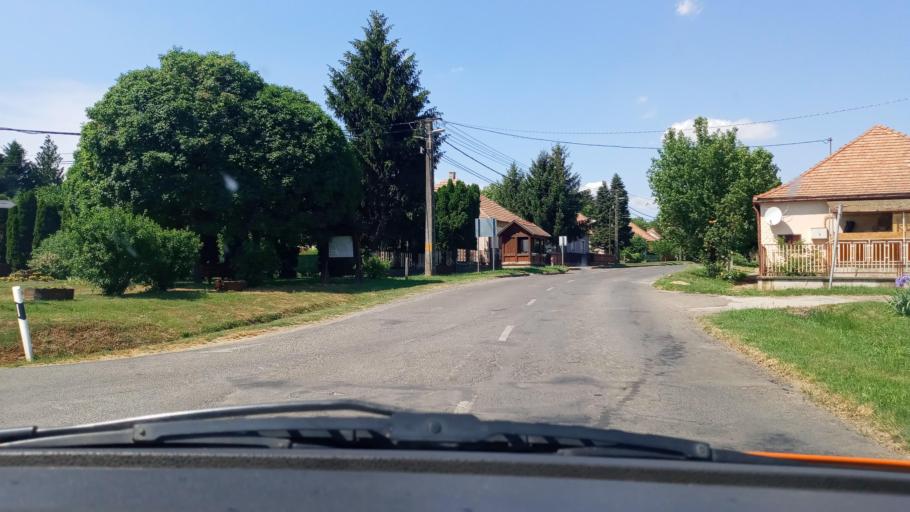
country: HU
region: Baranya
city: Harkany
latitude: 45.8770
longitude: 18.1709
